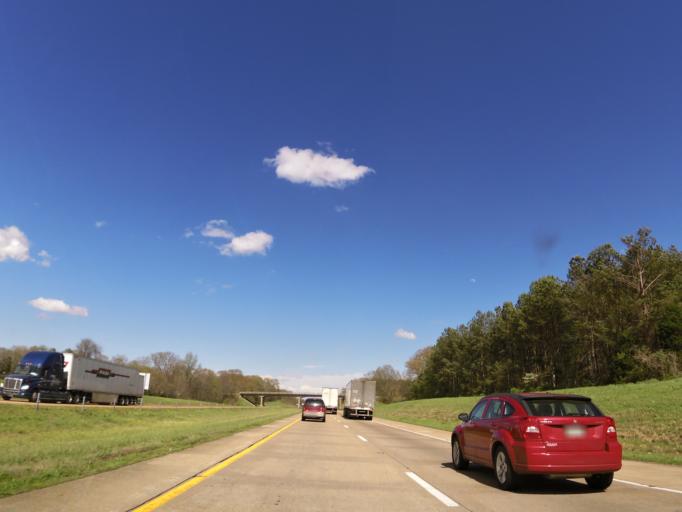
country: US
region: Tennessee
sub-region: Madison County
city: Jackson
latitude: 35.6887
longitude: -88.7161
